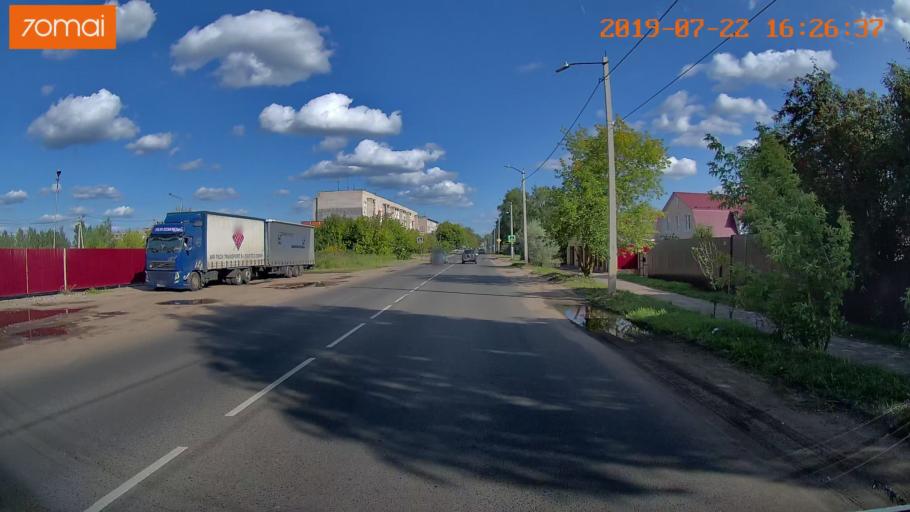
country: RU
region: Ivanovo
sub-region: Gorod Ivanovo
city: Ivanovo
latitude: 57.0482
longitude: 40.9365
